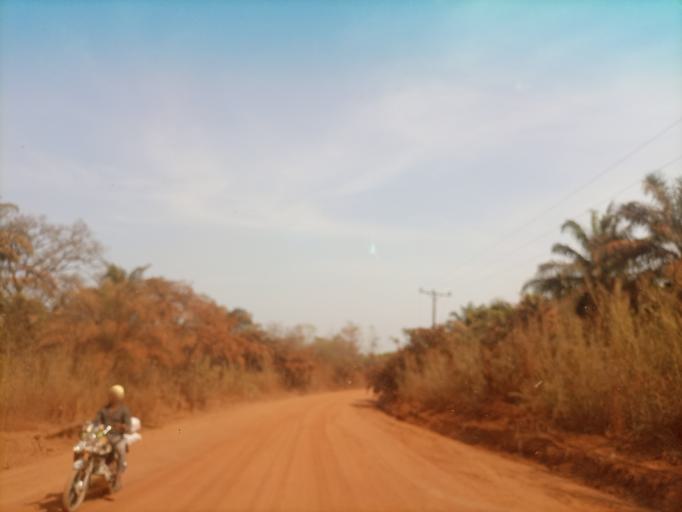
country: NG
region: Enugu
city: Eha Amufu
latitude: 6.6742
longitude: 7.7315
